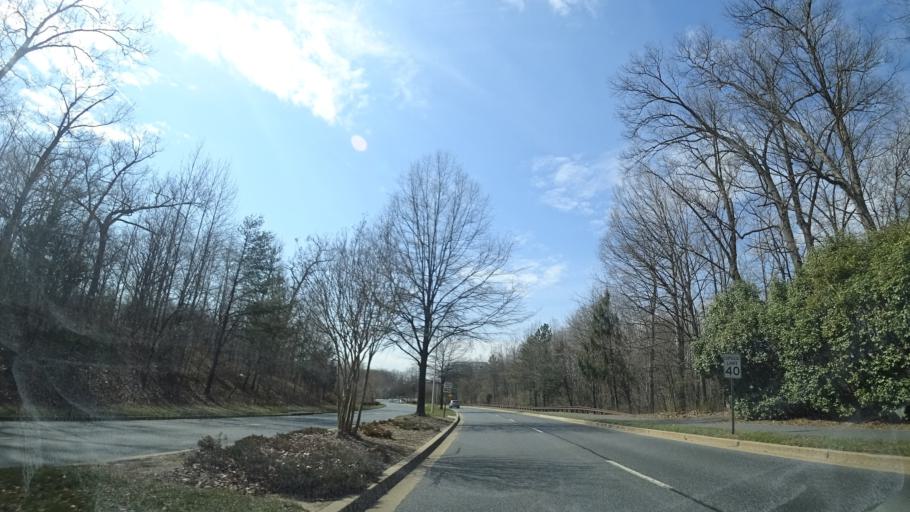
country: US
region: Maryland
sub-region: Montgomery County
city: Rockville
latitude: 39.0688
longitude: -77.1474
